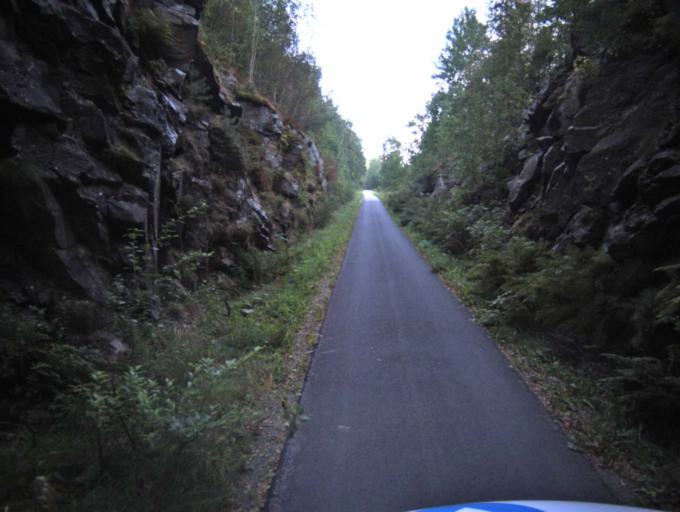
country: SE
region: Vaestra Goetaland
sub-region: Ulricehamns Kommun
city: Ulricehamn
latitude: 57.7542
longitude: 13.3966
